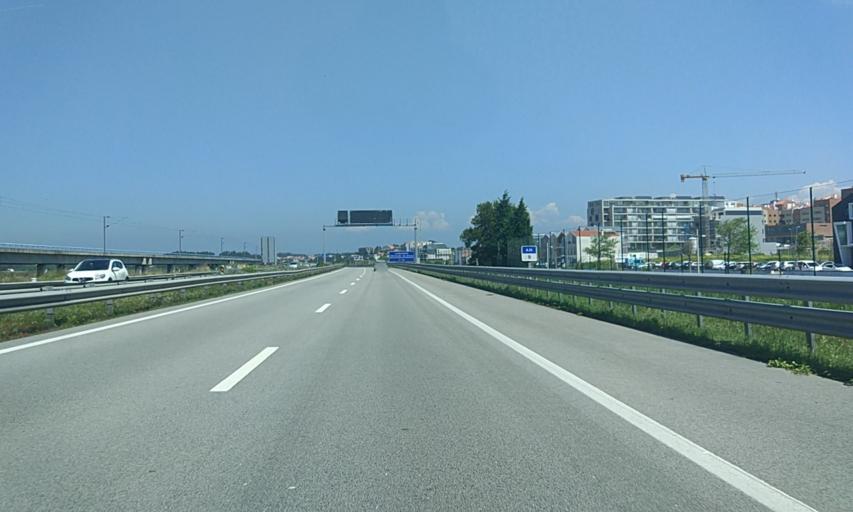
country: PT
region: Aveiro
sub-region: Aveiro
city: Aveiro
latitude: 40.6470
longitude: -8.6523
